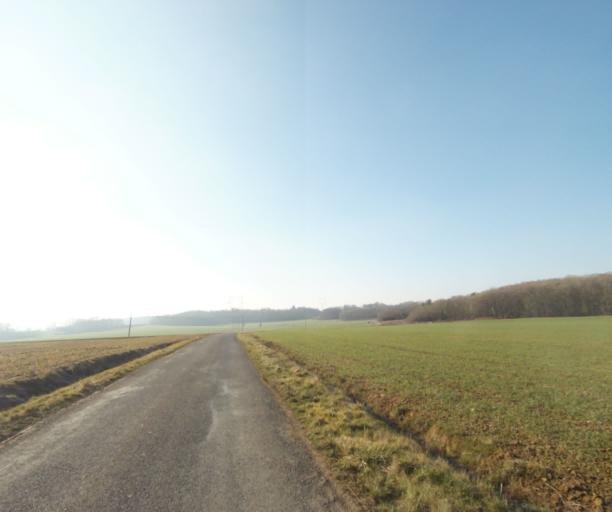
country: FR
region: Champagne-Ardenne
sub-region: Departement de la Haute-Marne
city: Wassy
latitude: 48.5193
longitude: 4.9841
